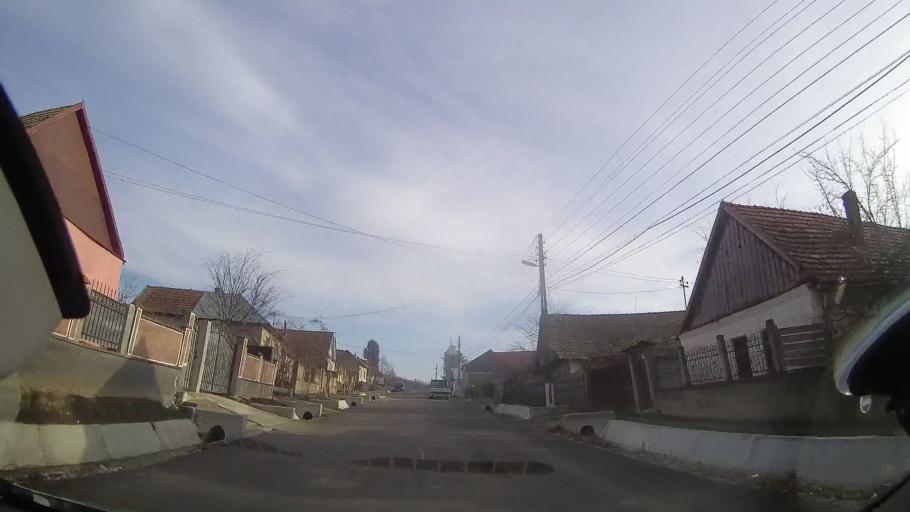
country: RO
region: Bihor
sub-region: Comuna Sarbi
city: Sarbi
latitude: 47.1775
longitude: 22.1462
